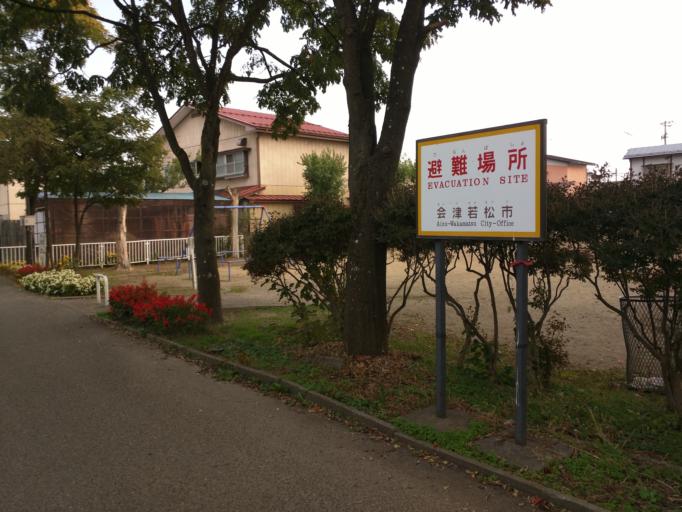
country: JP
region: Fukushima
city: Kitakata
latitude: 37.4912
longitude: 139.9074
